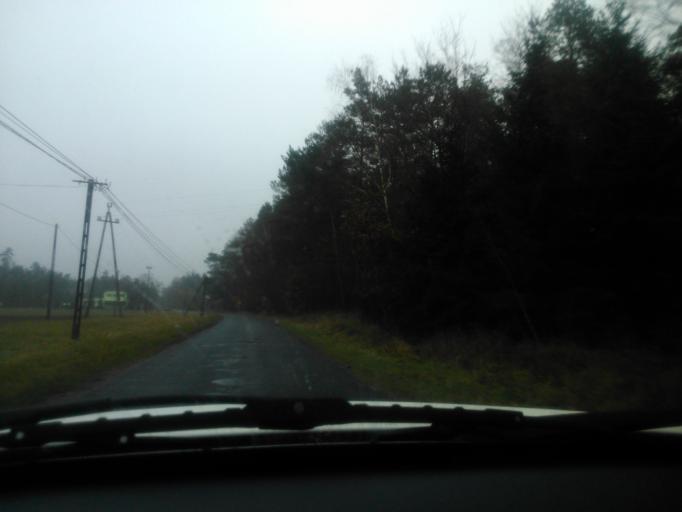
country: PL
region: Kujawsko-Pomorskie
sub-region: Powiat golubsko-dobrzynski
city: Golub-Dobrzyn
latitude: 53.1466
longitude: 19.1317
